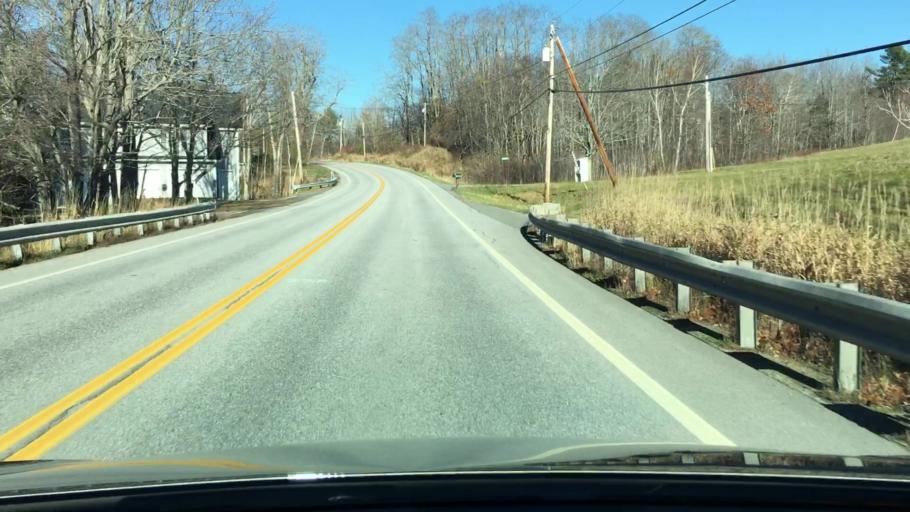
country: US
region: Maine
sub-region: Waldo County
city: Winterport
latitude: 44.6397
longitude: -68.8276
